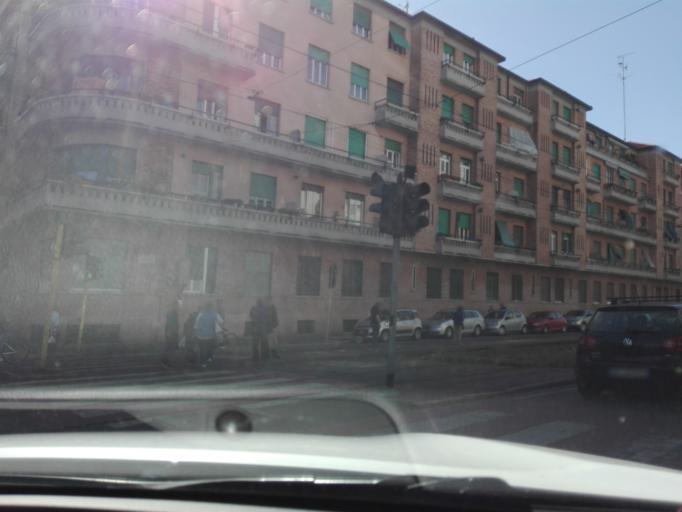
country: IT
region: Lombardy
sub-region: Citta metropolitana di Milano
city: Romano Banco
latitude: 45.4725
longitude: 9.1429
